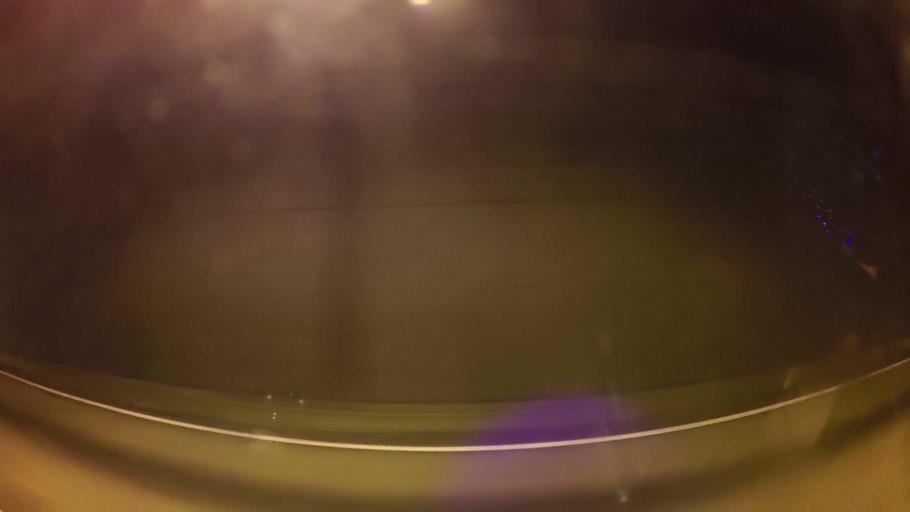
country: CL
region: Valparaiso
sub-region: Provincia de Valparaiso
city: Valparaiso
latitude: -33.0292
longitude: -71.6520
